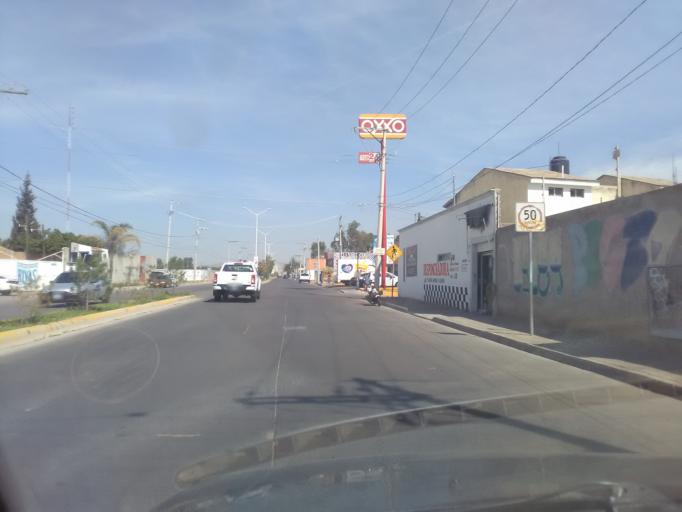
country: MX
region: Durango
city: Victoria de Durango
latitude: 24.0495
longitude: -104.6252
